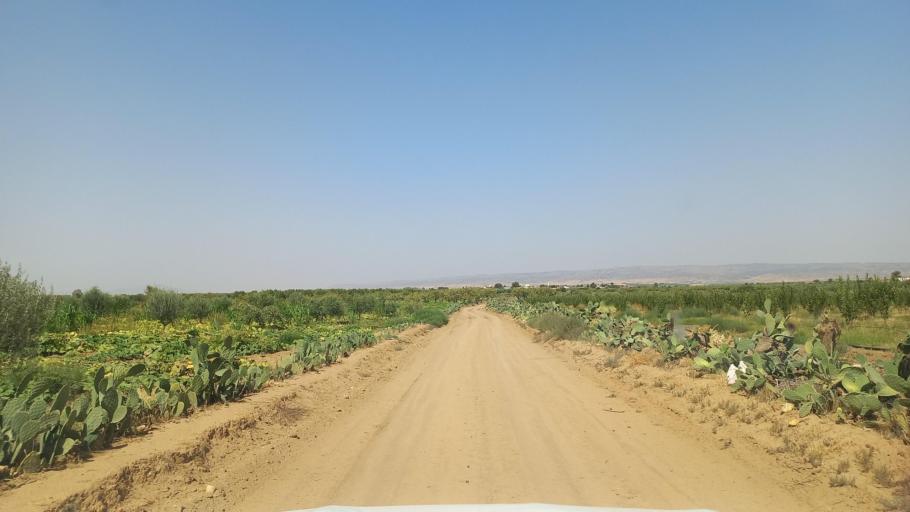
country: TN
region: Al Qasrayn
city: Kasserine
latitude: 35.2457
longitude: 9.0412
